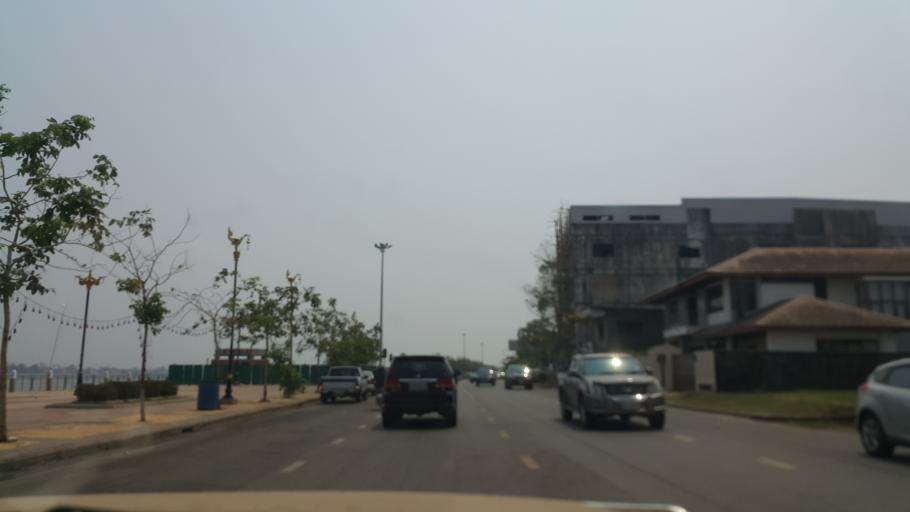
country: TH
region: Nakhon Phanom
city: Nakhon Phanom
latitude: 17.4000
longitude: 104.7898
